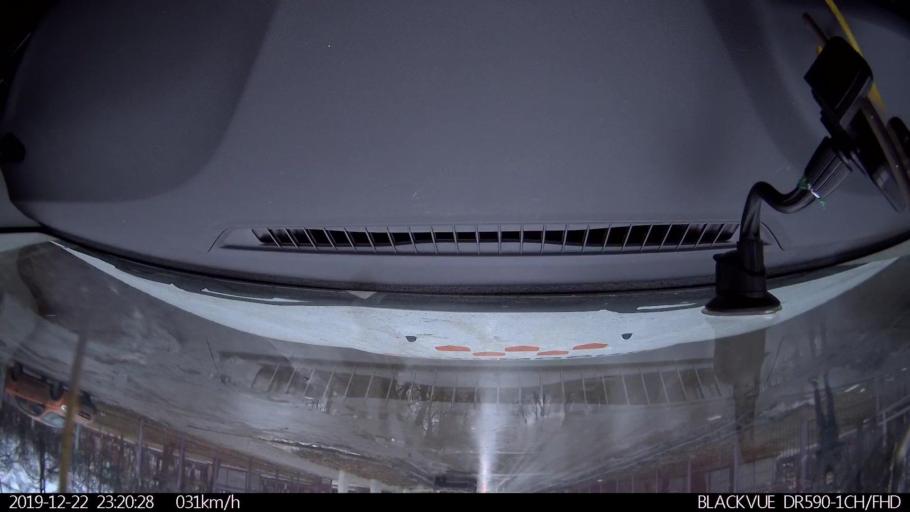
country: RU
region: Nizjnij Novgorod
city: Gorbatovka
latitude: 56.2458
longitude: 43.8605
